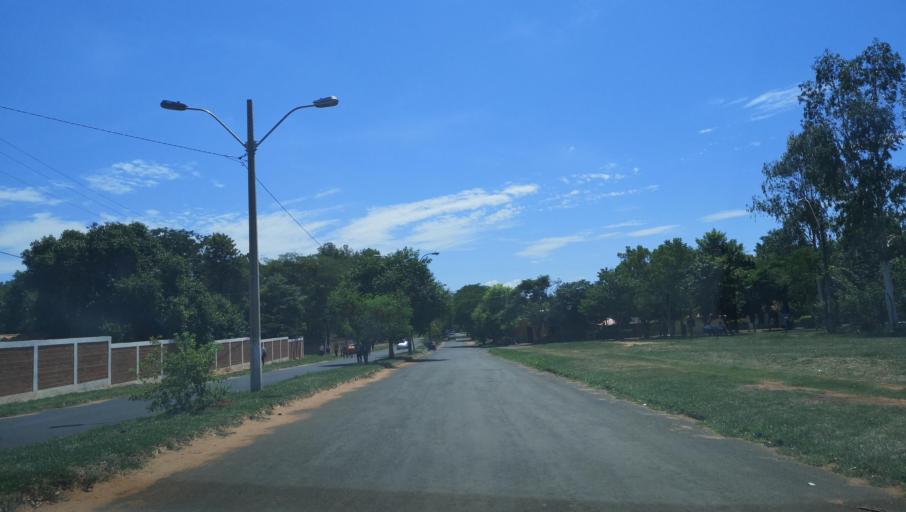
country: PY
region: Misiones
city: Santa Maria
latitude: -26.8936
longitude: -57.0314
